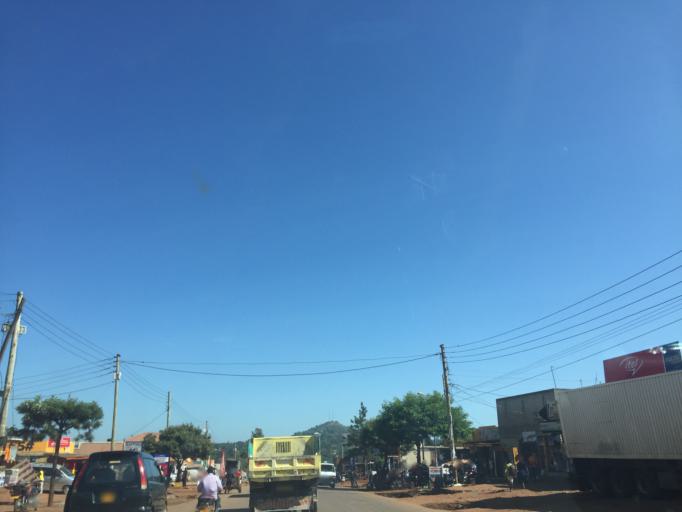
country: UG
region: Central Region
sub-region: Luwero District
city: Wobulenzi
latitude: 0.7190
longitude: 32.5282
